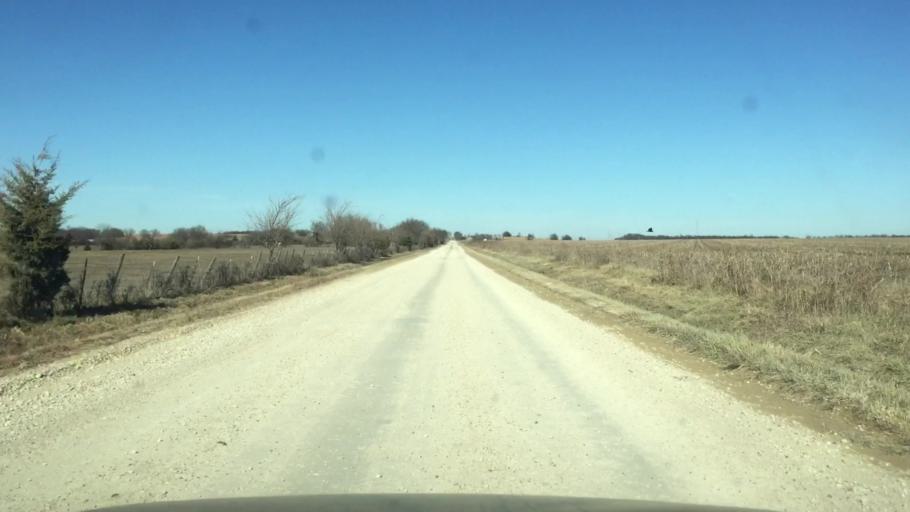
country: US
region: Kansas
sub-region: Allen County
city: Iola
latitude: 37.8641
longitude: -95.3914
